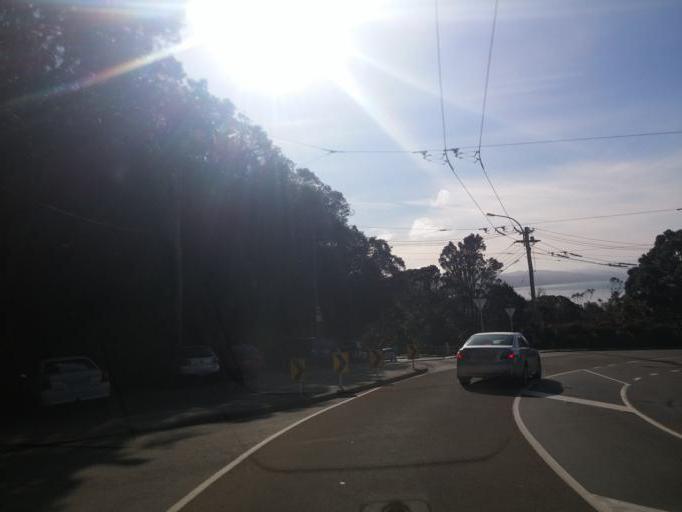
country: NZ
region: Wellington
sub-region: Wellington City
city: Brooklyn
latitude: -41.3030
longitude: 174.7640
